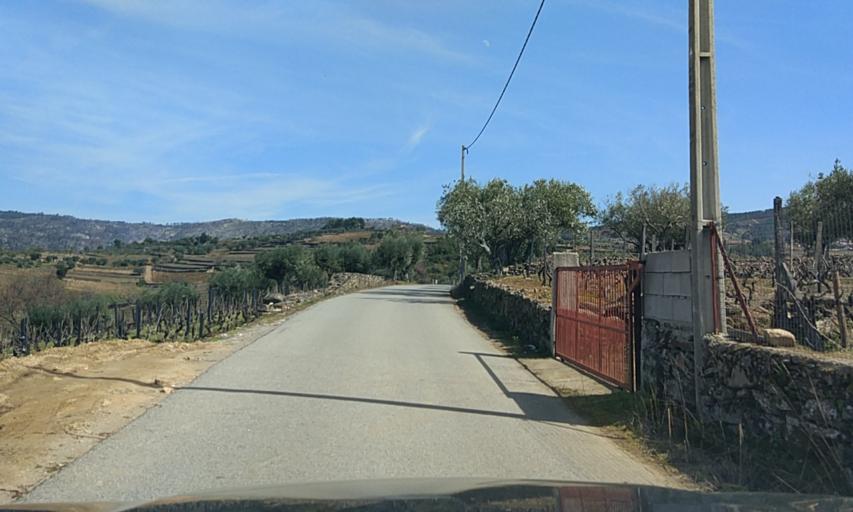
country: PT
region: Vila Real
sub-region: Sabrosa
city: Sabrosa
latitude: 41.2977
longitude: -7.5378
